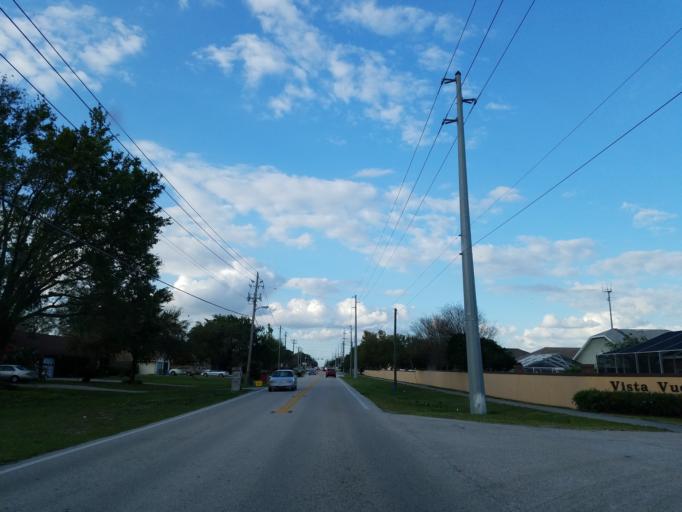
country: US
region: Florida
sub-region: Polk County
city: Lakeland Highlands
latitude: 27.9496
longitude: -81.9236
